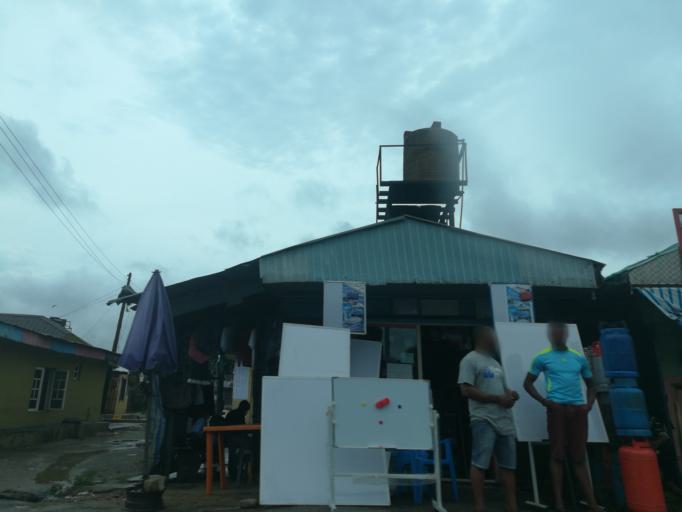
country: NG
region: Rivers
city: Port Harcourt
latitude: 4.8559
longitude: 7.0311
